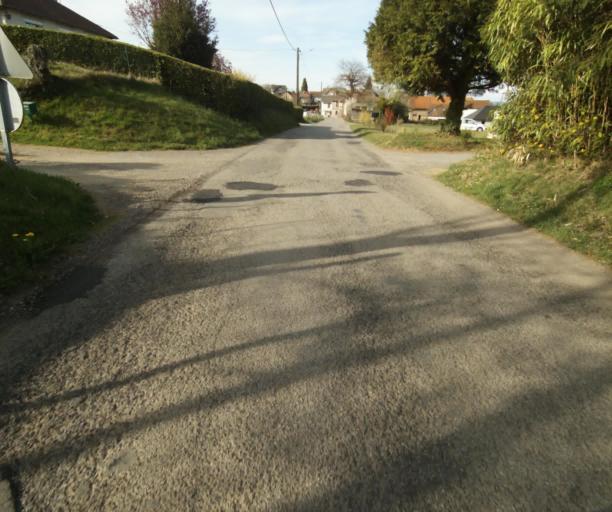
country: FR
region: Limousin
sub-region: Departement de la Correze
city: Naves
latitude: 45.2946
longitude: 1.7404
